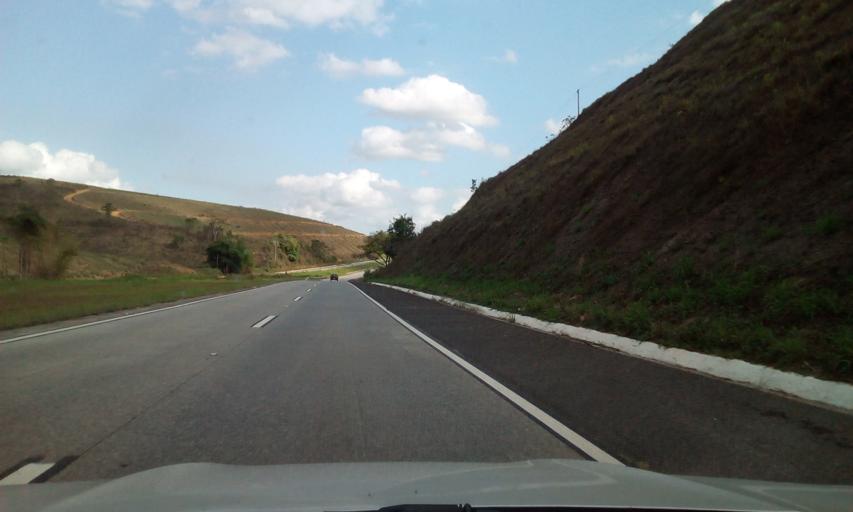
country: BR
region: Pernambuco
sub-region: Gameleira
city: Gameleira
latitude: -8.5553
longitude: -35.4320
